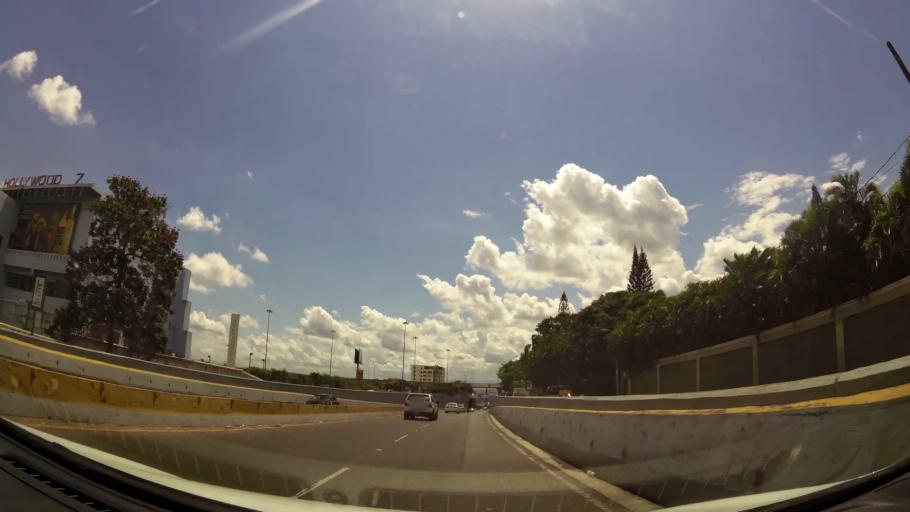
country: DO
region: Santiago
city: Santiago de los Caballeros
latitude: 19.4523
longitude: -70.6856
